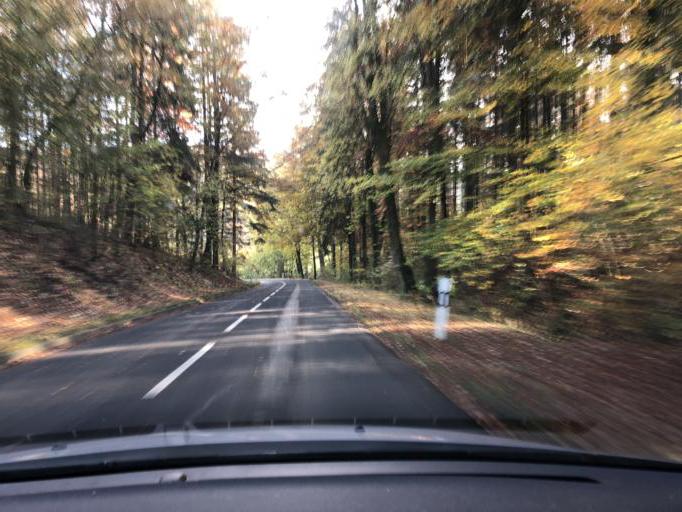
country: DE
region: Thuringia
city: Reurieth
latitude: 50.4382
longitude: 10.6448
